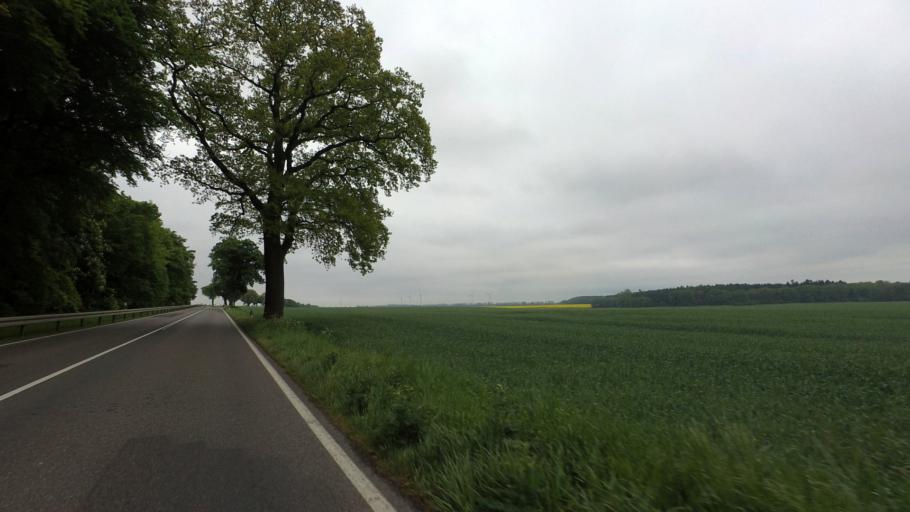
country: DE
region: Mecklenburg-Vorpommern
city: Penzlin
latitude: 53.5131
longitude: 13.0371
